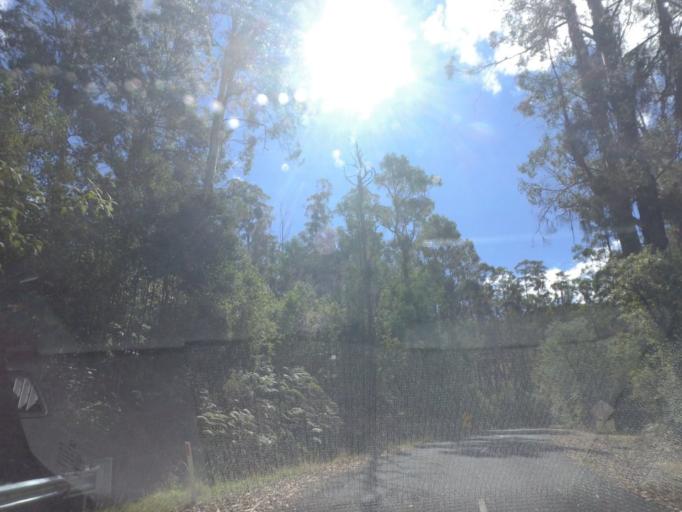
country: AU
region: Victoria
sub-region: Murrindindi
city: Alexandra
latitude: -37.3276
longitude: 145.9321
